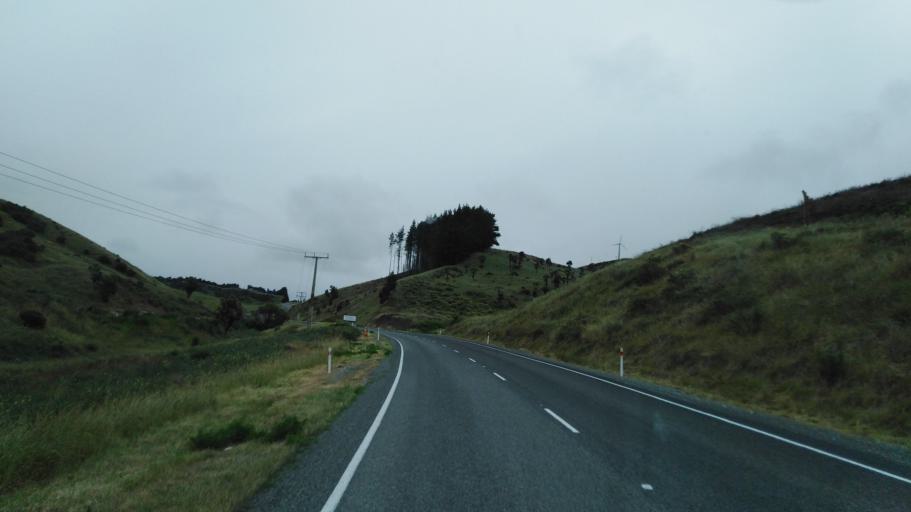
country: NZ
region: Marlborough
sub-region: Marlborough District
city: Blenheim
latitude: -41.8958
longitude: 174.1162
